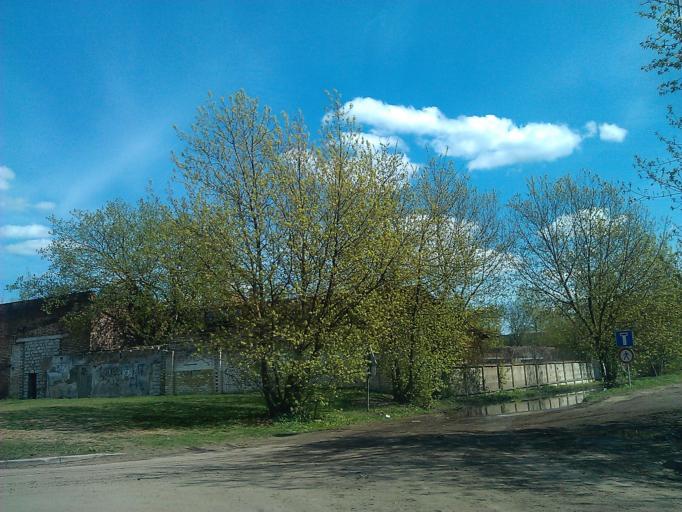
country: LV
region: Riga
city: Riga
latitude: 56.9387
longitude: 24.1344
